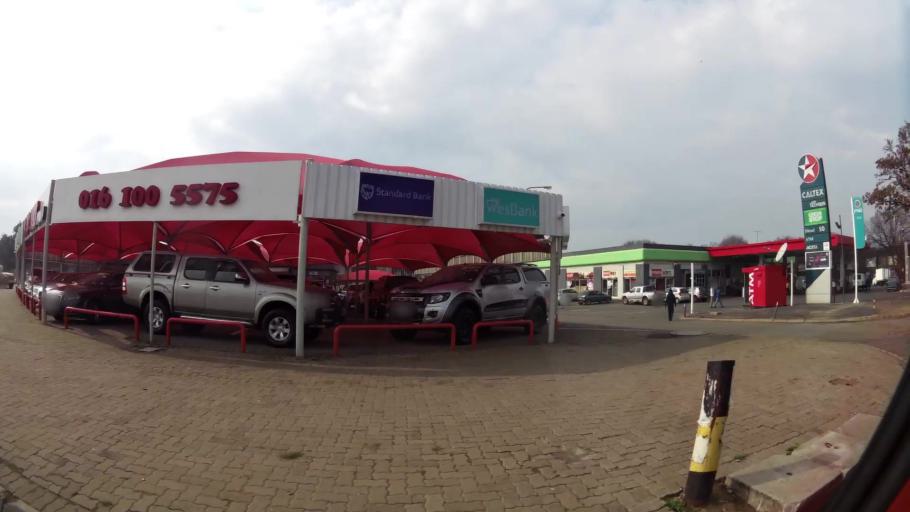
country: ZA
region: Gauteng
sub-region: Sedibeng District Municipality
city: Vanderbijlpark
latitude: -26.6841
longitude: 27.8349
